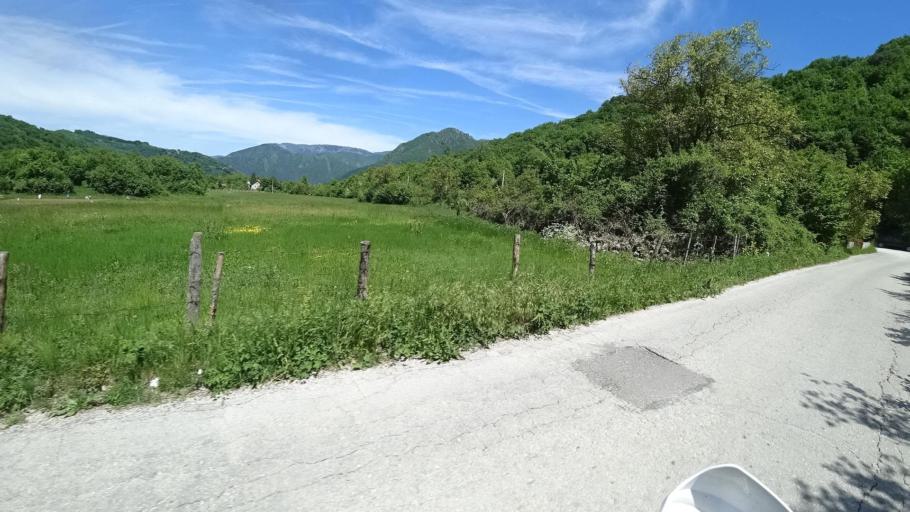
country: BA
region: Federation of Bosnia and Herzegovina
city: Bijela
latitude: 43.6104
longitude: 17.9538
